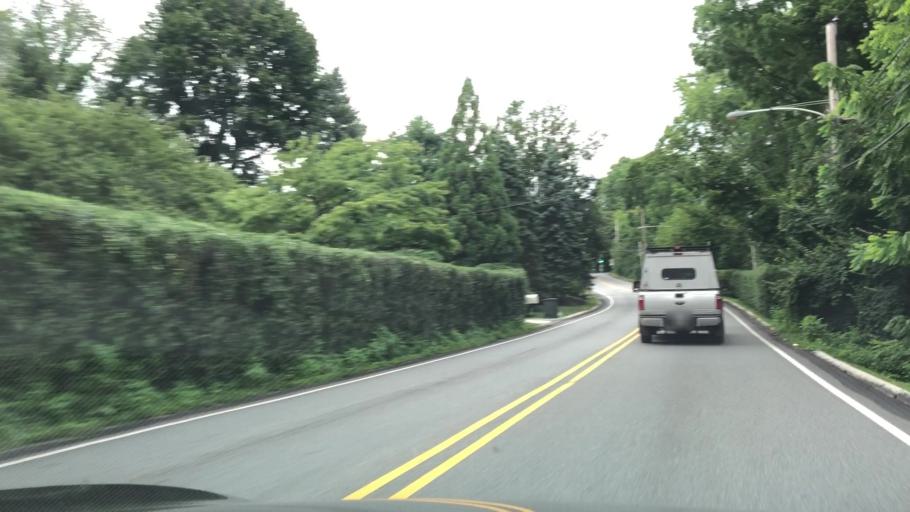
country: US
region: Pennsylvania
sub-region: Chester County
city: Devon
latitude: 40.0501
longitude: -75.4258
